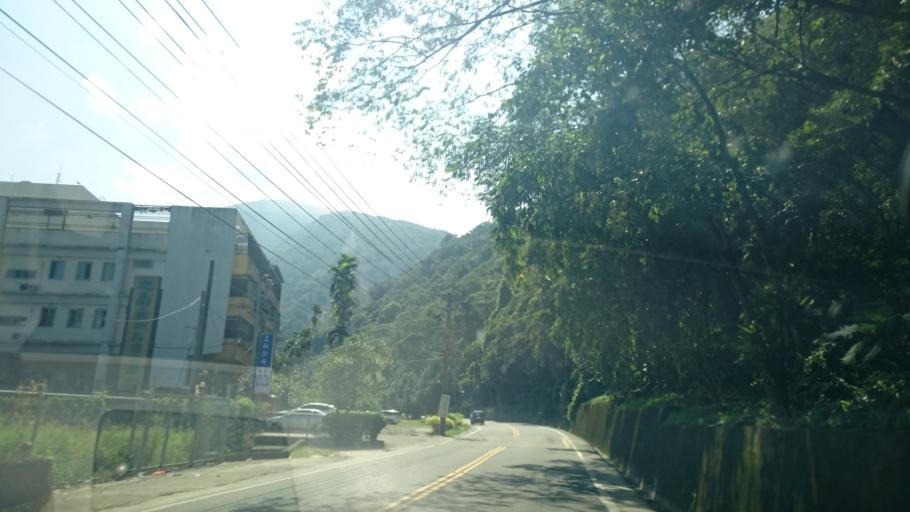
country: TW
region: Taiwan
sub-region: Nantou
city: Puli
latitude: 23.9779
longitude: 121.0023
